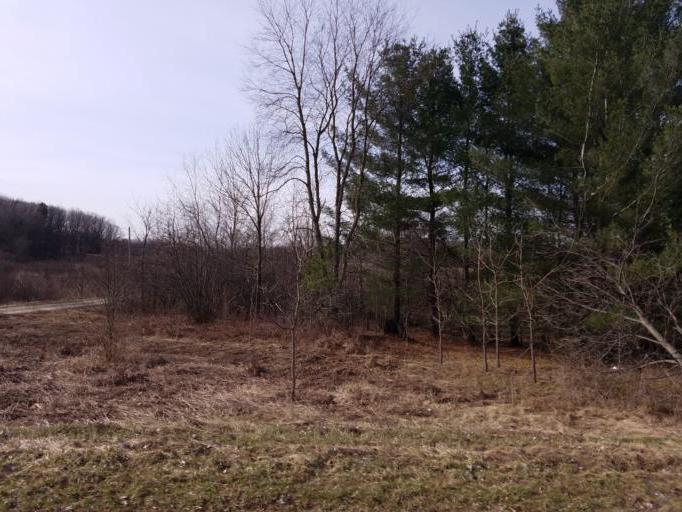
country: US
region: Michigan
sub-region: Montcalm County
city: Howard City
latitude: 43.5260
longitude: -85.4708
